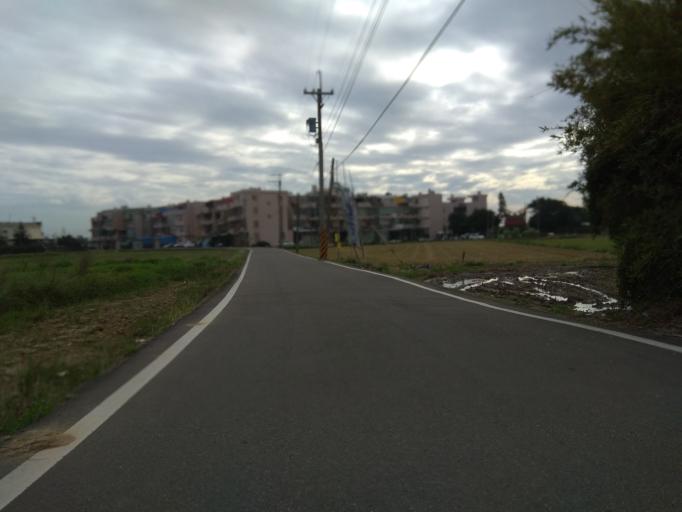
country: TW
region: Taiwan
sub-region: Hsinchu
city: Zhubei
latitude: 24.9839
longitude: 121.0541
